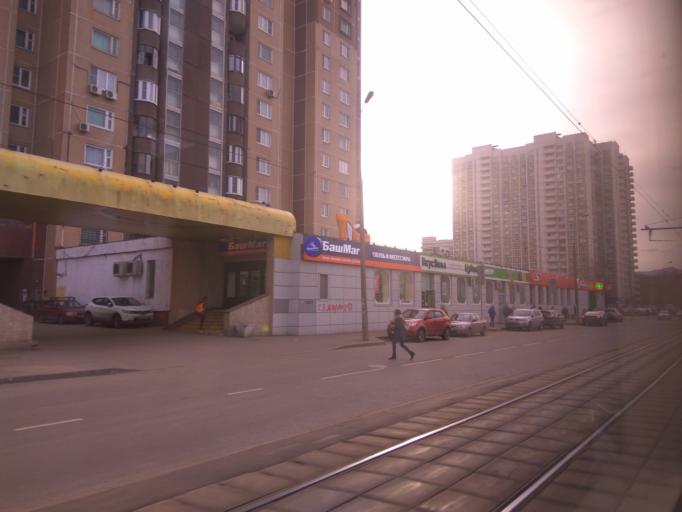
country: RU
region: Moscow
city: Leonovo
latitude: 55.8702
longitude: 37.6599
